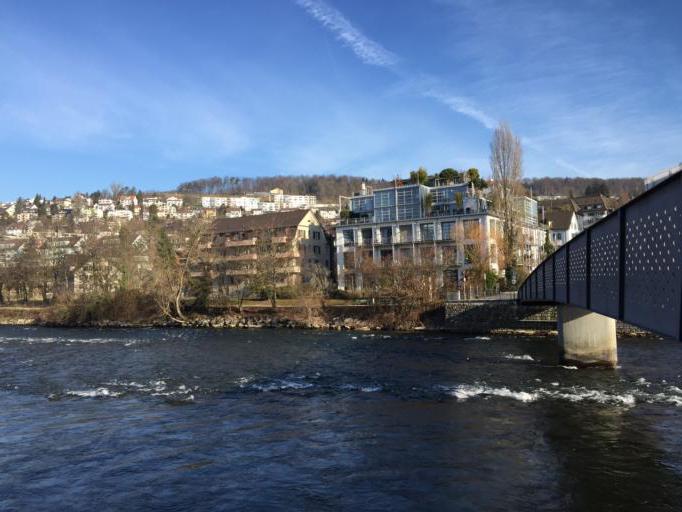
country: CH
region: Zurich
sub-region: Bezirk Zuerich
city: Zuerich (Kreis 5)
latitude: 47.3923
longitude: 8.5191
